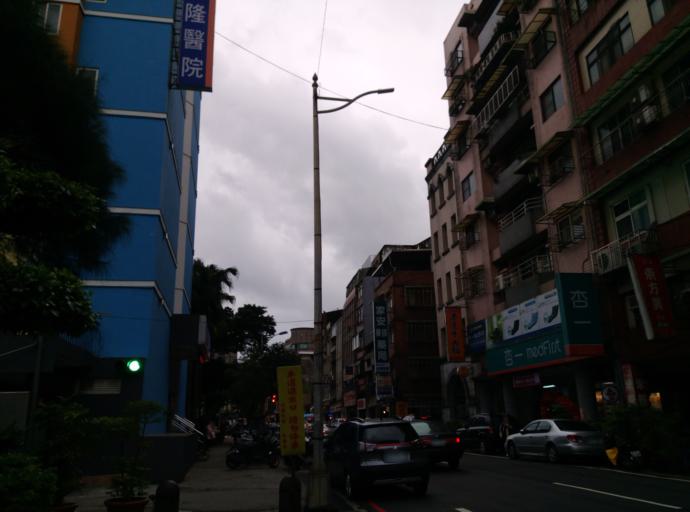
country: TW
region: Taiwan
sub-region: Keelung
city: Keelung
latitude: 25.1303
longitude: 121.7474
